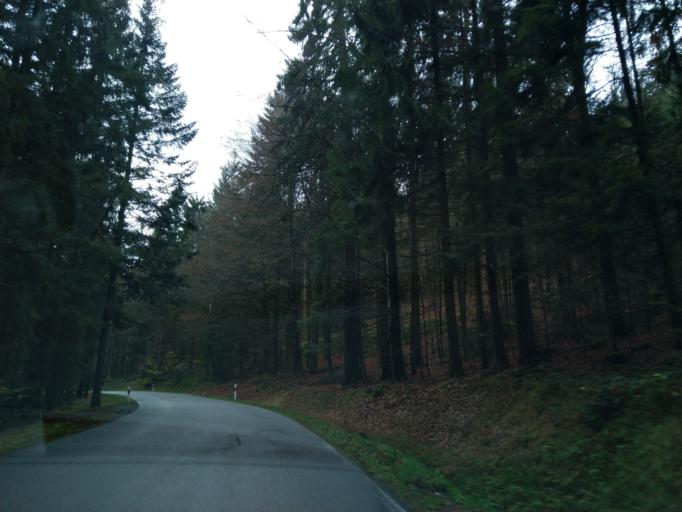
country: DE
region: Bavaria
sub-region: Lower Bavaria
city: Schofweg
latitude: 48.8318
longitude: 13.2248
